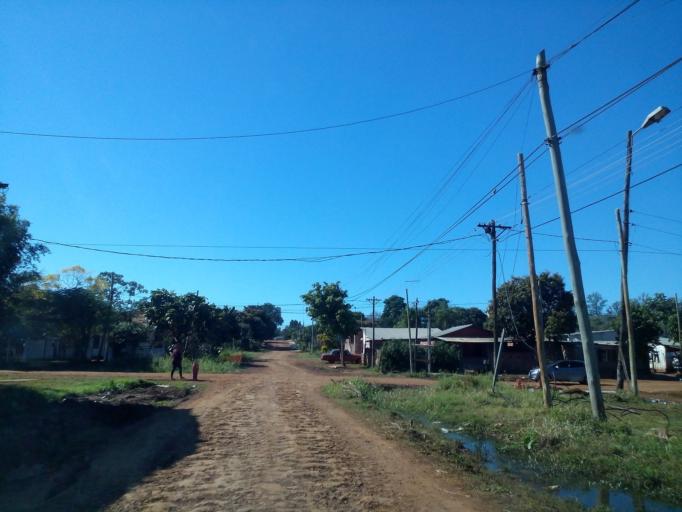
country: AR
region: Misiones
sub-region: Departamento de Capital
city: Posadas
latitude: -27.3910
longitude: -55.9241
